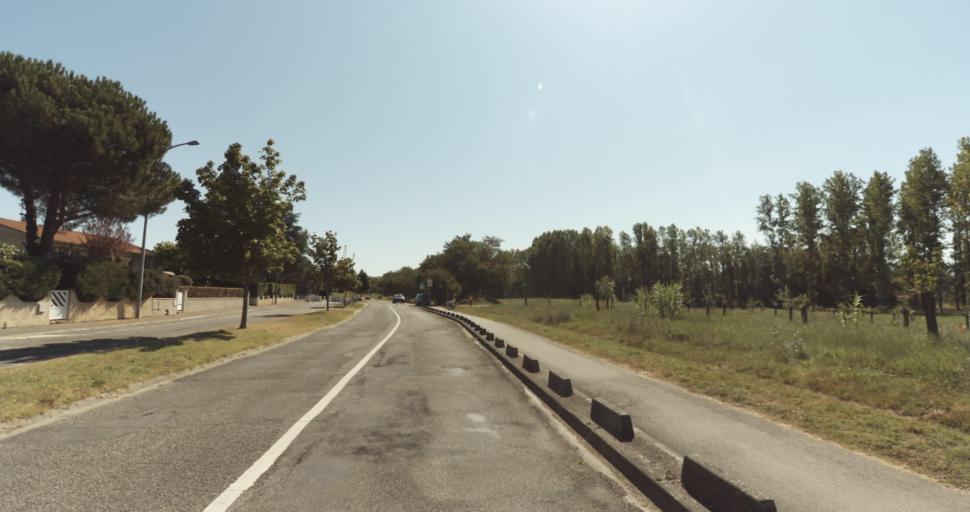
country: FR
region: Midi-Pyrenees
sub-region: Departement de la Haute-Garonne
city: Saint-Jean
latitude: 43.6478
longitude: 1.4987
